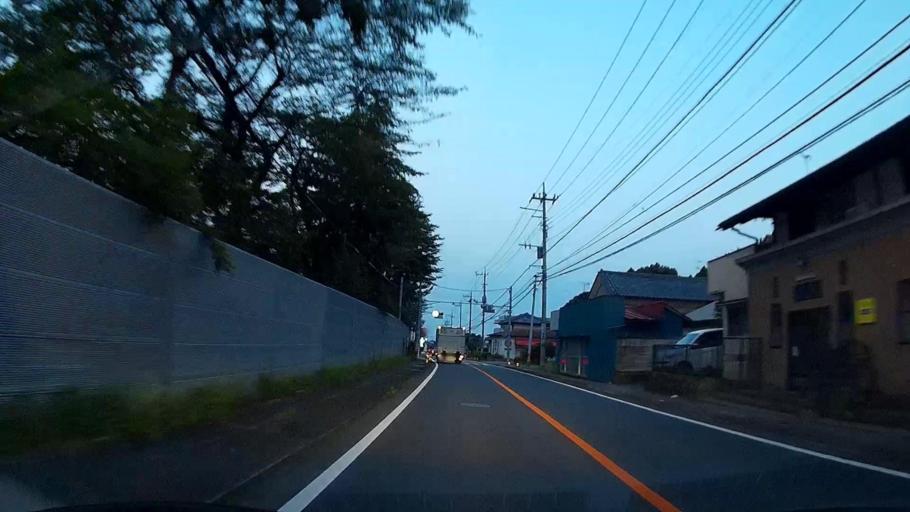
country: JP
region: Gunma
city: Annaka
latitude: 36.3743
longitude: 138.8964
